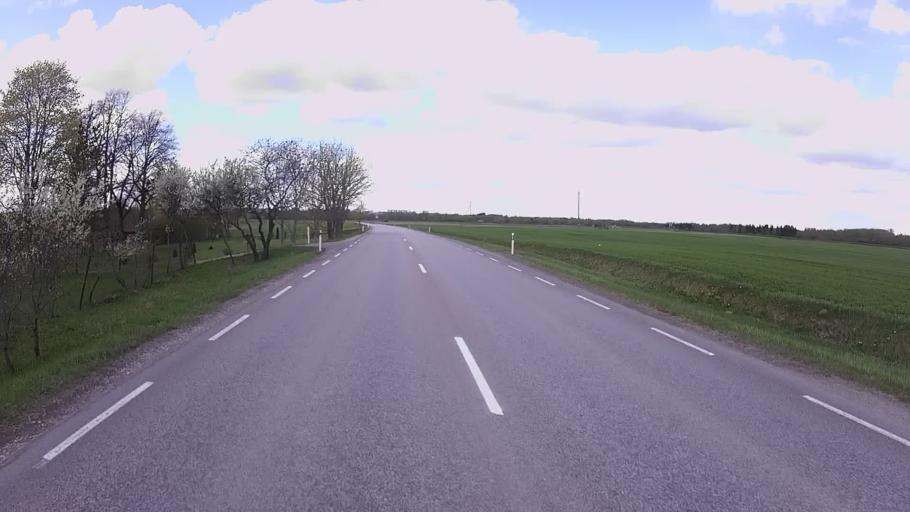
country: EE
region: Jogevamaa
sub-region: Jogeva linn
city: Jogeva
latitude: 58.7060
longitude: 26.4234
